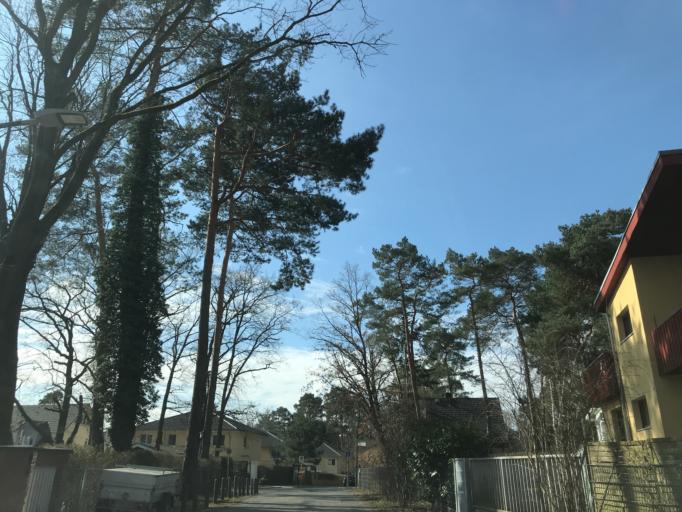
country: DE
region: Berlin
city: Kladow
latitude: 52.4510
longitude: 13.1190
